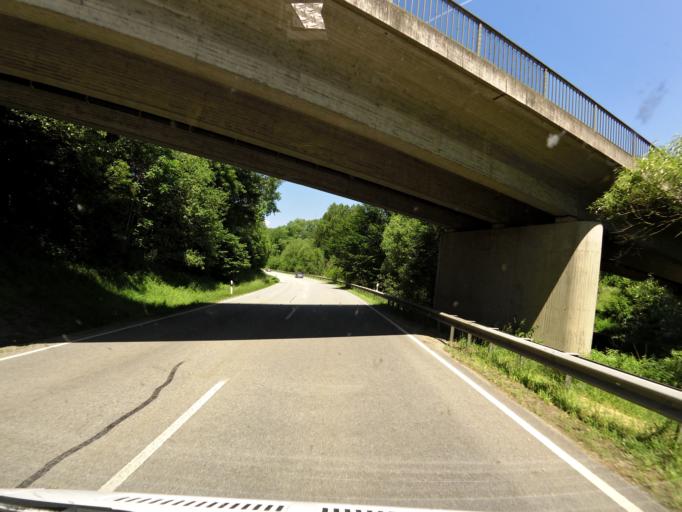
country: DE
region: Bavaria
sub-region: Lower Bavaria
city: Roehrnbach
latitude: 48.7383
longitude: 13.5192
